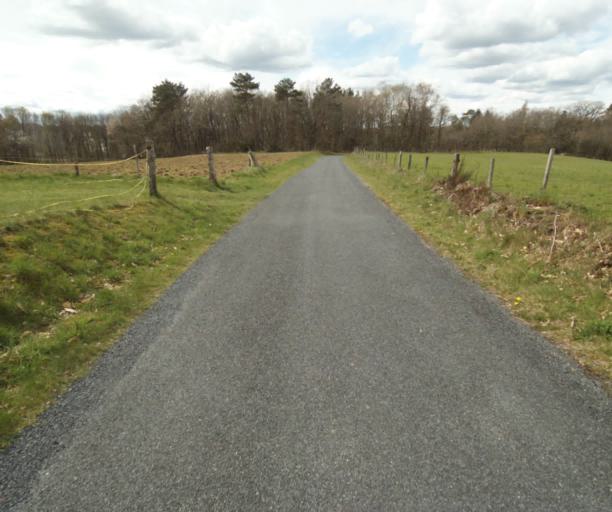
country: FR
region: Limousin
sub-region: Departement de la Correze
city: Laguenne
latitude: 45.2201
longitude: 1.9021
